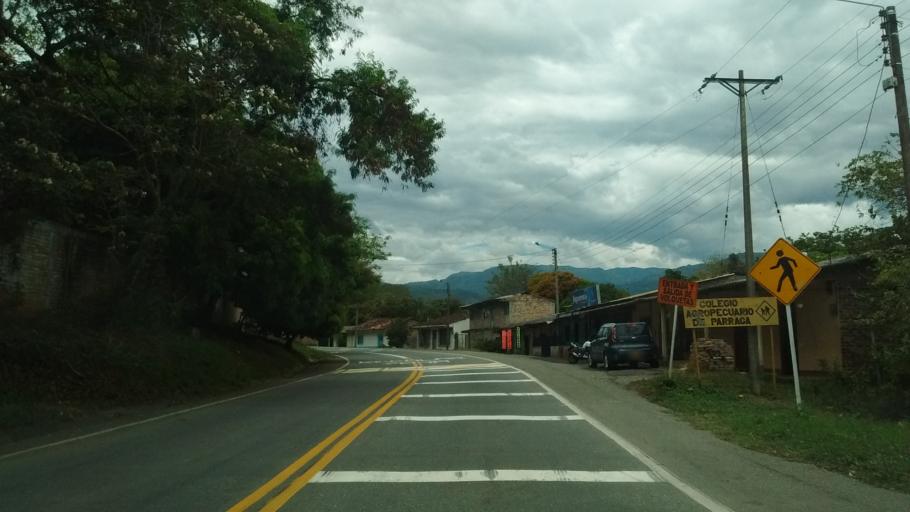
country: CO
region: Cauca
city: Rosas
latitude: 2.2303
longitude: -76.7882
